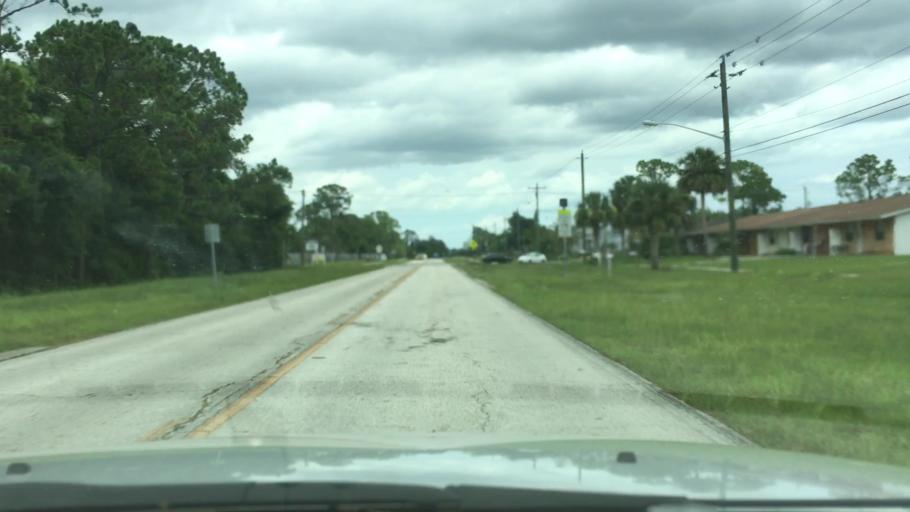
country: US
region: Florida
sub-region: Volusia County
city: Holly Hill
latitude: 29.2220
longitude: -81.0704
